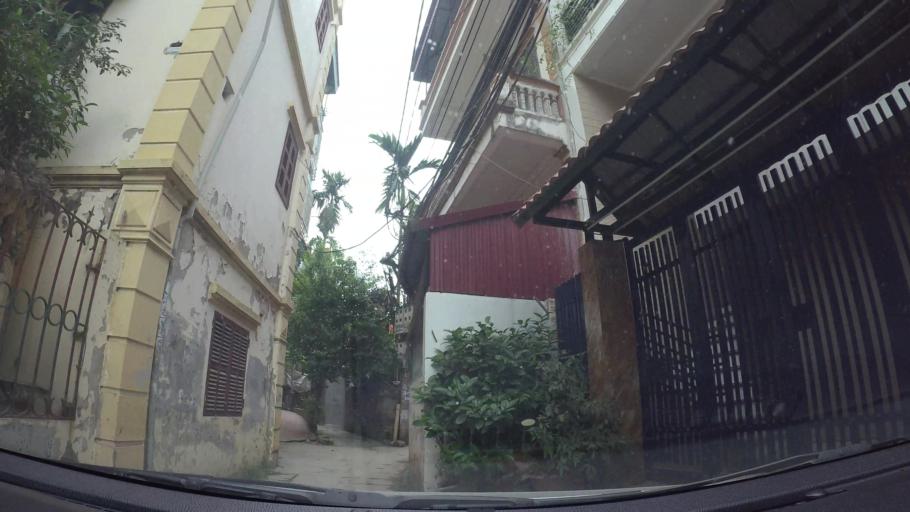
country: VN
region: Ha Noi
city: Tay Ho
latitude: 21.0781
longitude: 105.8216
